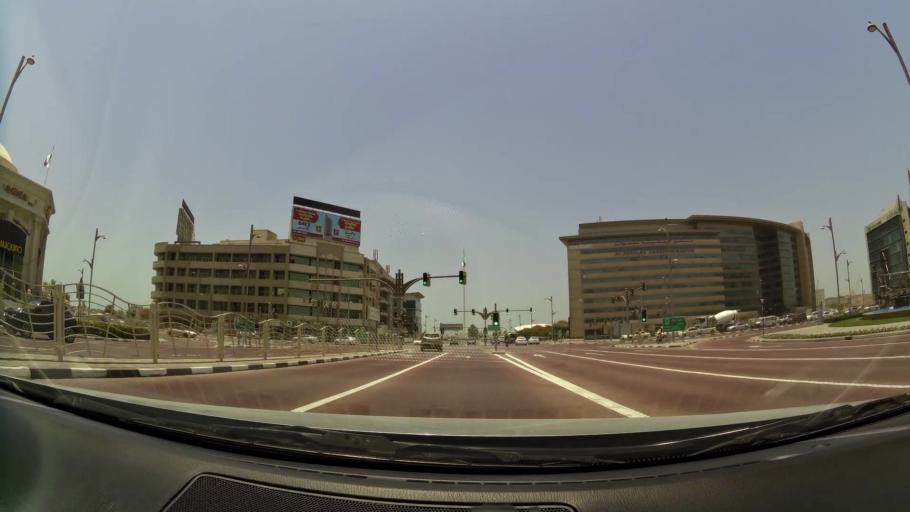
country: AE
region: Ash Shariqah
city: Sharjah
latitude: 25.2387
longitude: 55.2732
